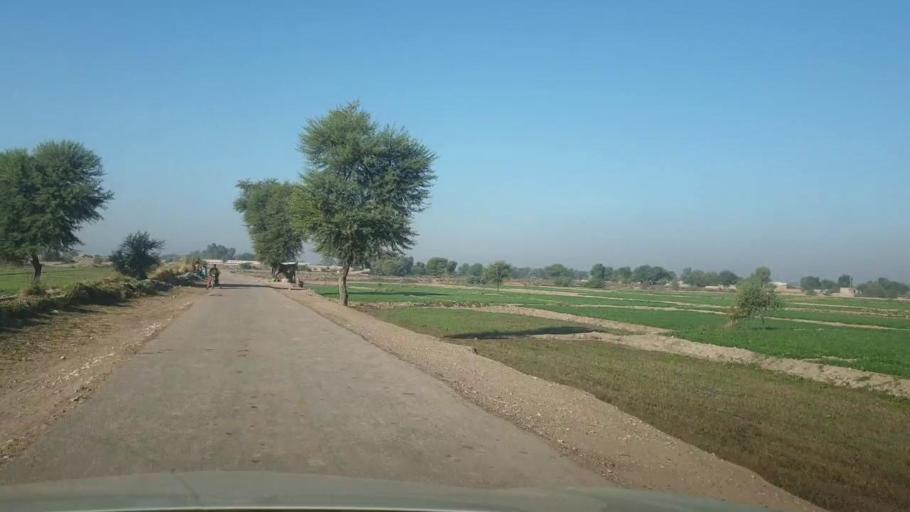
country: PK
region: Sindh
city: Bhan
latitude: 26.5534
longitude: 67.6913
